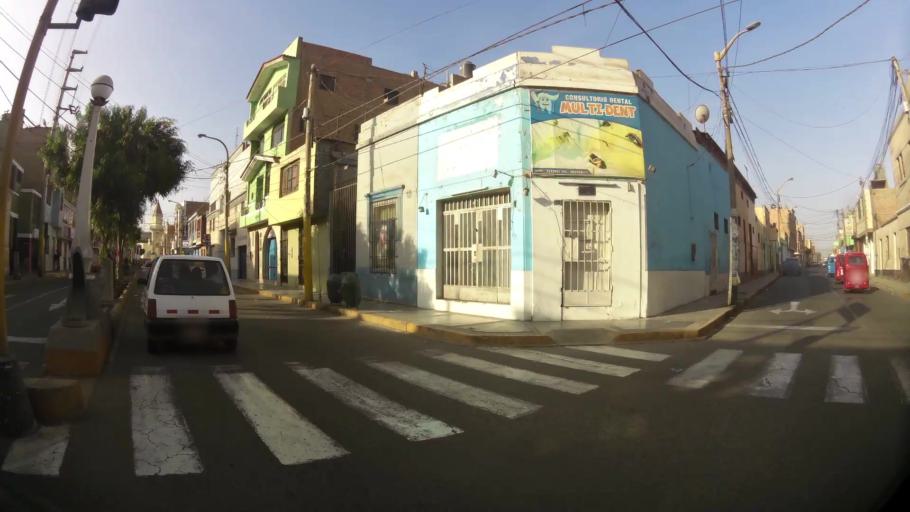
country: PE
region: Lima
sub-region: Huaura
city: Huacho
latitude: -11.1102
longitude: -77.6100
